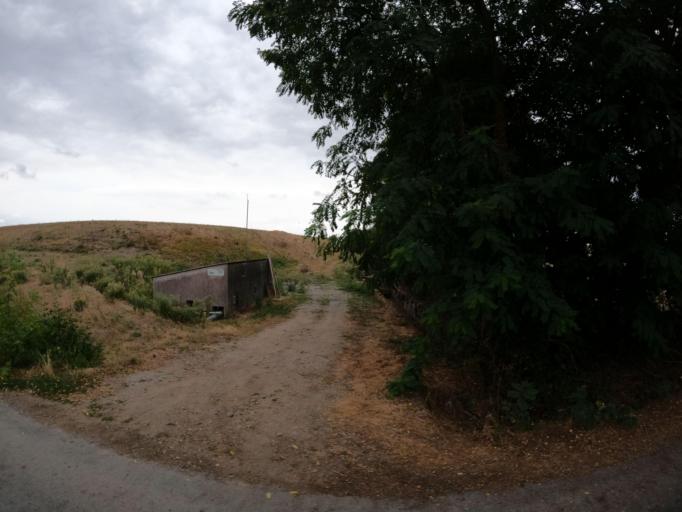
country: FR
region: Pays de la Loire
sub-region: Departement de la Vendee
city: La Bruffiere
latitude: 46.9869
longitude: -1.1630
